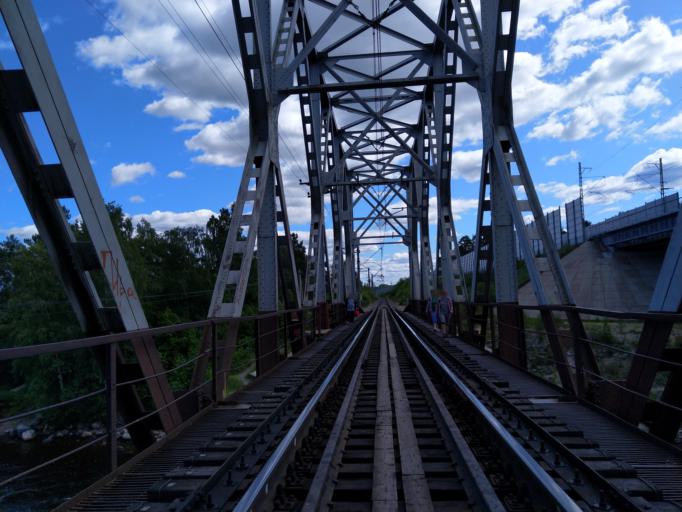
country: RU
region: Leningrad
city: Sapernoye
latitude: 60.6822
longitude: 30.0089
